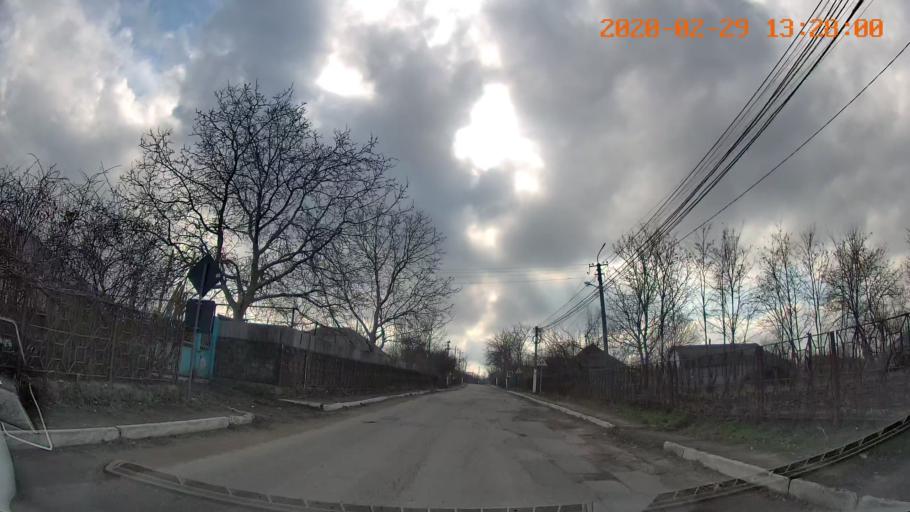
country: MD
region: Telenesti
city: Camenca
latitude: 47.9087
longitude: 28.6444
